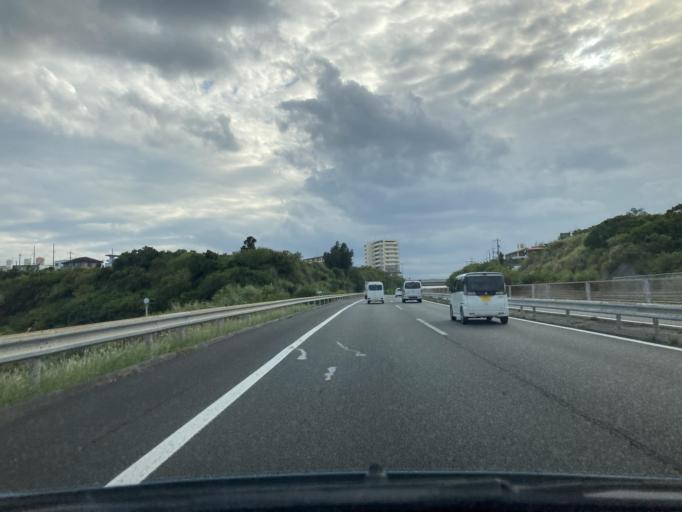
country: JP
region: Okinawa
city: Ginowan
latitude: 26.2605
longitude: 127.7708
